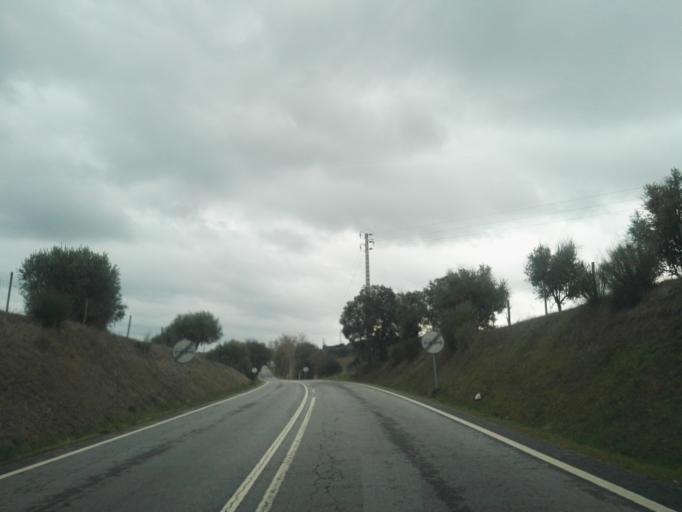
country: PT
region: Portalegre
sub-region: Arronches
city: Arronches
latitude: 39.1186
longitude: -7.2936
